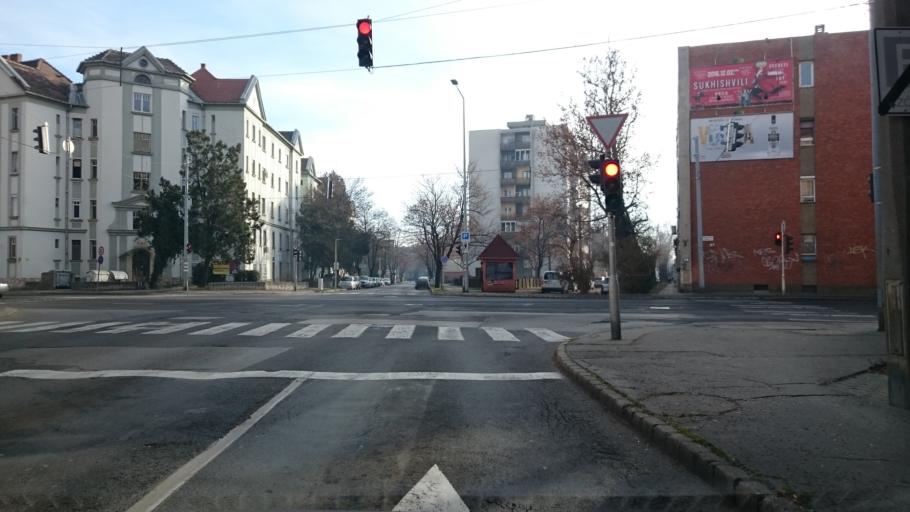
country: HU
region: Baranya
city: Pecs
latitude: 46.0713
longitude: 18.2171
